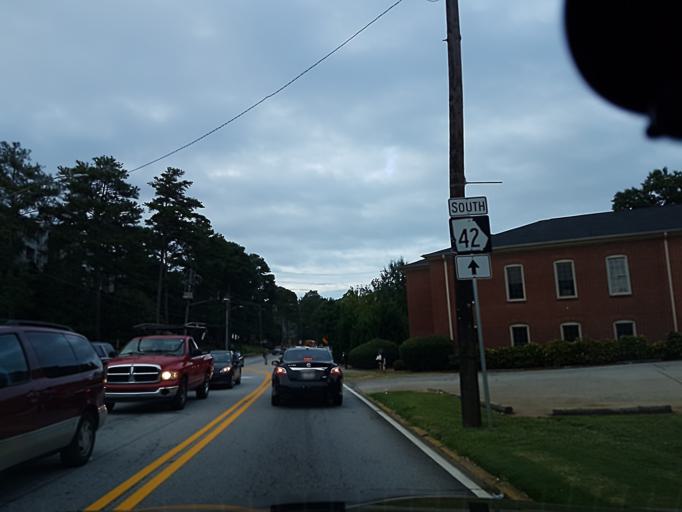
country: US
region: Georgia
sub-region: DeKalb County
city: North Druid Hills
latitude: 33.8154
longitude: -84.3347
